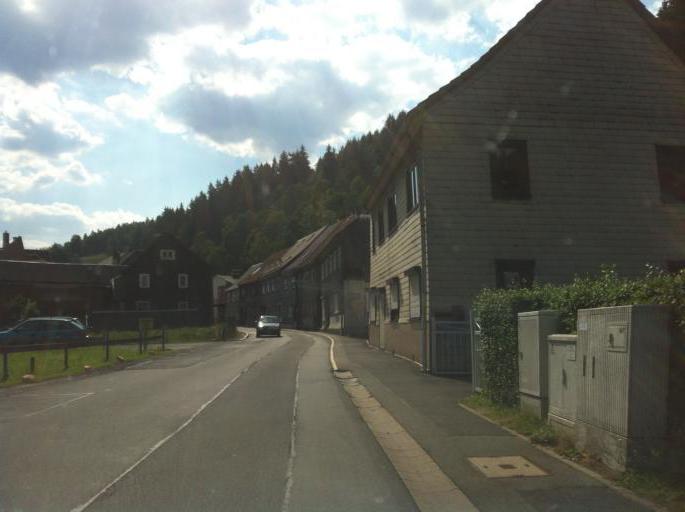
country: DE
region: Thuringia
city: Goldisthal
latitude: 50.5410
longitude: 11.0212
